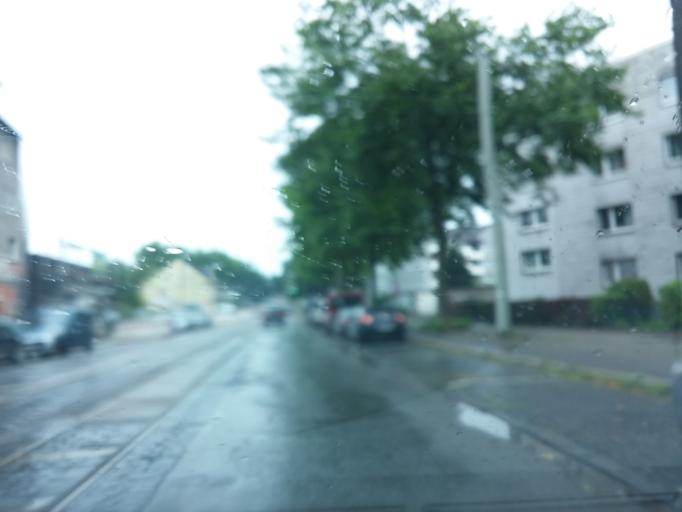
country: DE
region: North Rhine-Westphalia
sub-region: Regierungsbezirk Munster
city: Gladbeck
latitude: 51.5621
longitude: 7.0465
